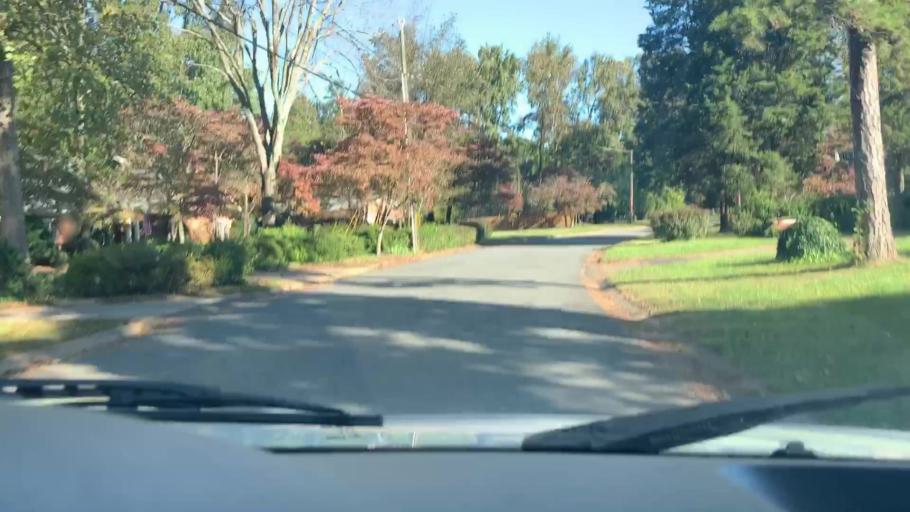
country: US
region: North Carolina
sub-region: Mecklenburg County
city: Charlotte
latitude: 35.2895
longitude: -80.7929
